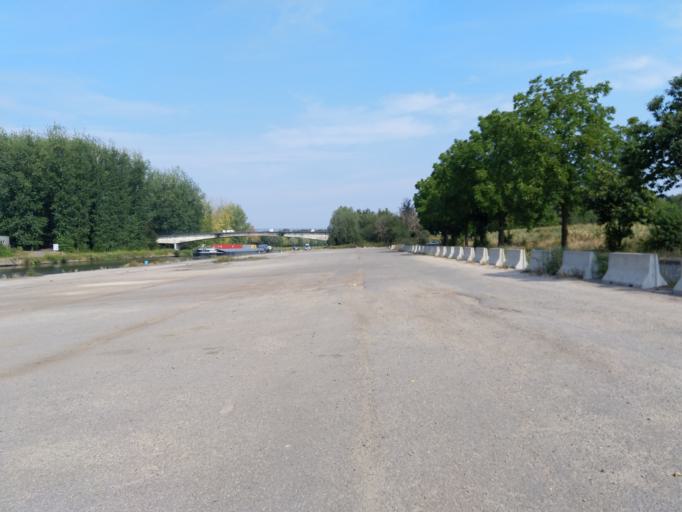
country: BE
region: Wallonia
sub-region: Province du Hainaut
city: Seneffe
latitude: 50.5233
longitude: 4.2453
